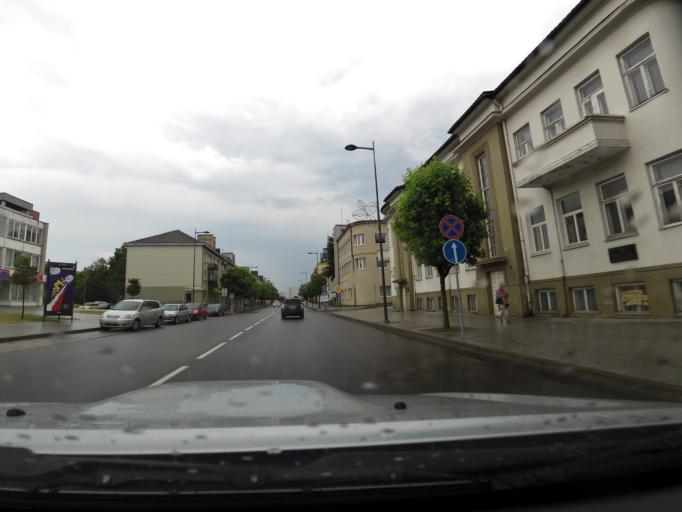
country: LT
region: Marijampoles apskritis
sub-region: Marijampole Municipality
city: Marijampole
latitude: 54.5534
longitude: 23.3487
